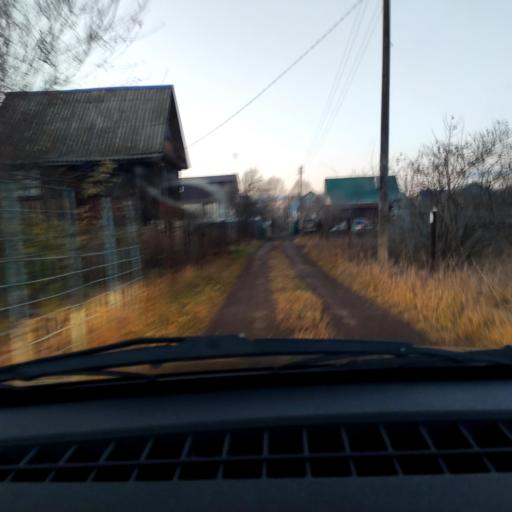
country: RU
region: Bashkortostan
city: Ufa
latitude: 54.6491
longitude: 55.8988
